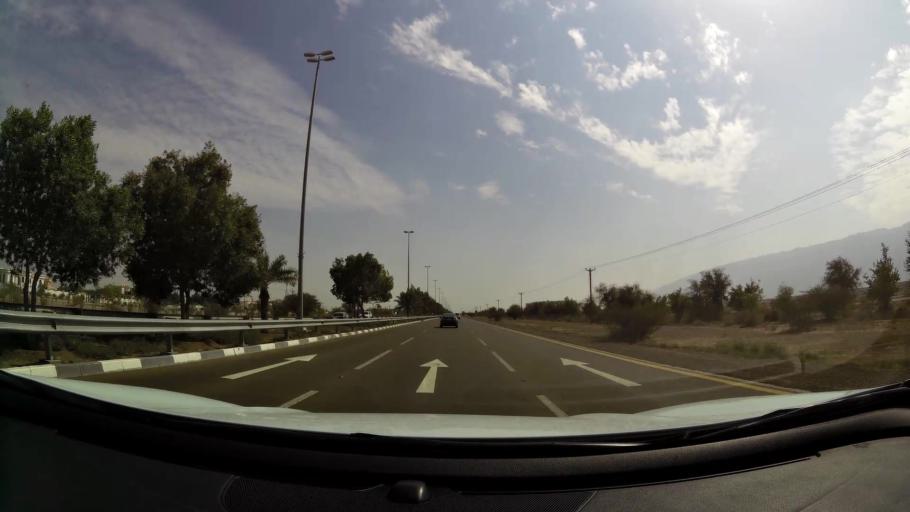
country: AE
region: Abu Dhabi
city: Al Ain
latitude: 24.0934
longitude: 55.8299
